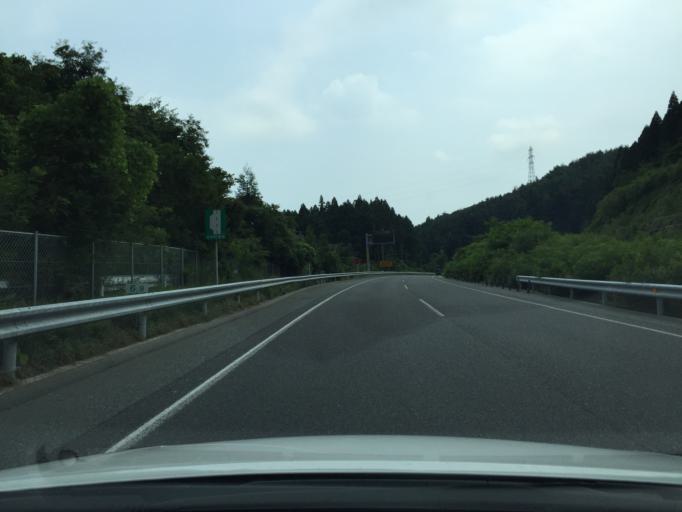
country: JP
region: Fukushima
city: Iwaki
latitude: 37.0924
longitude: 140.7856
